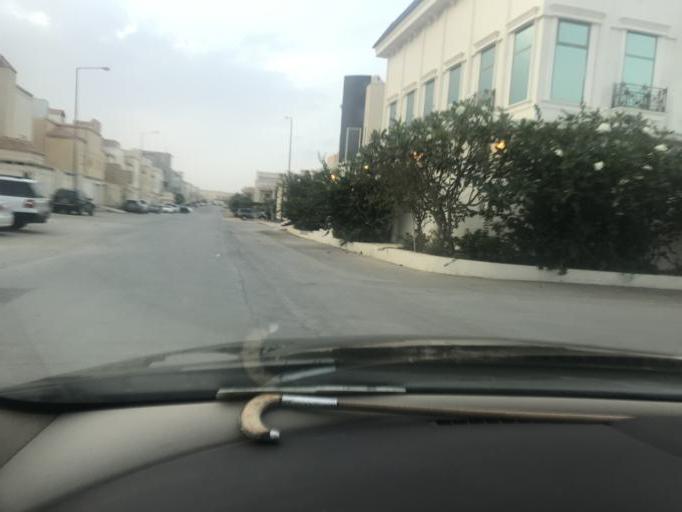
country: SA
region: Ar Riyad
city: Riyadh
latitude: 24.7301
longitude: 46.7445
